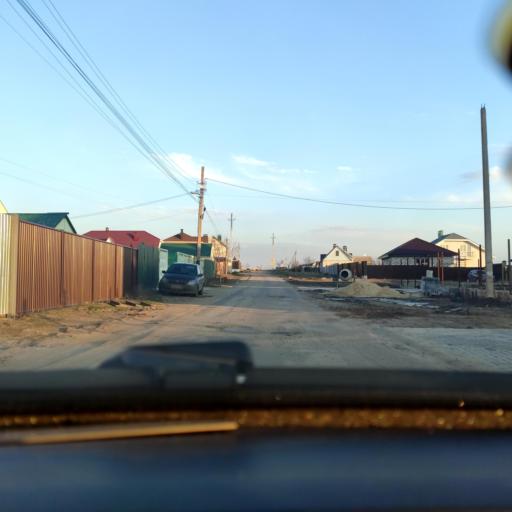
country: RU
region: Voronezj
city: Shilovo
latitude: 51.5791
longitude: 39.0388
